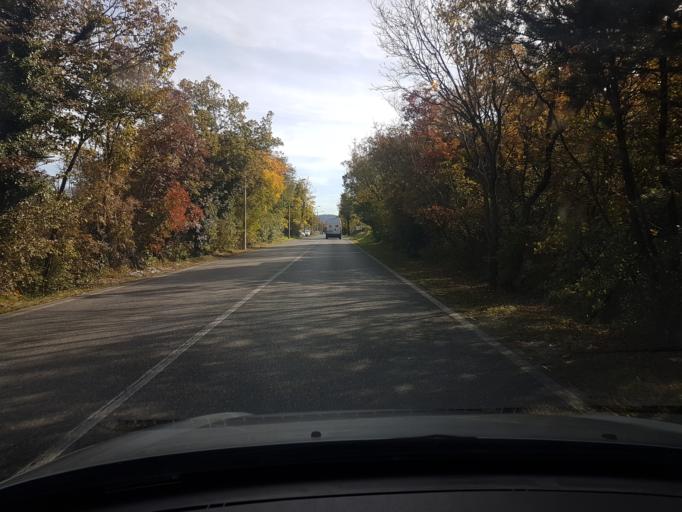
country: IT
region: Friuli Venezia Giulia
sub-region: Provincia di Trieste
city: Prosecco-Contovello
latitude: 45.7193
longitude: 13.7222
